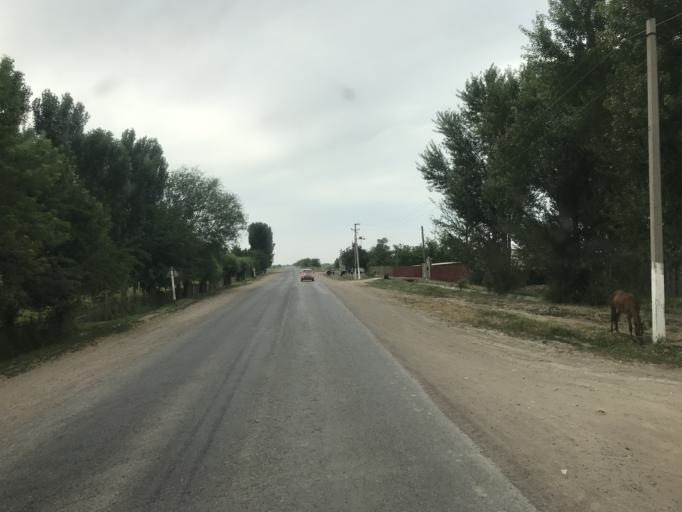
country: KZ
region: Ongtustik Qazaqstan
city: Asykata
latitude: 40.9063
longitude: 68.3536
